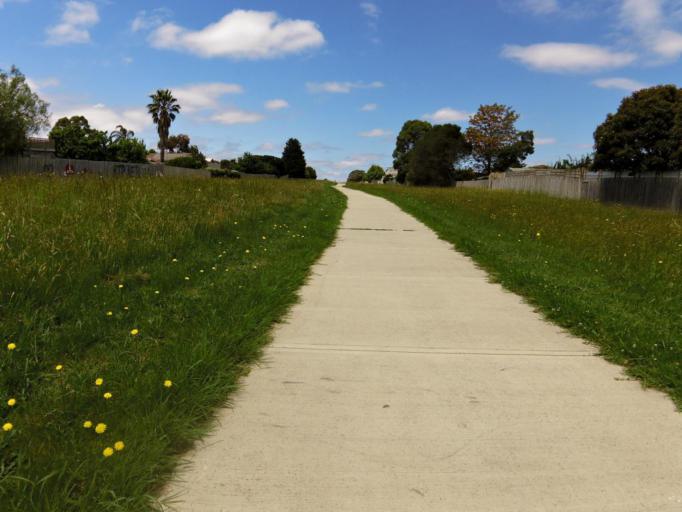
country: AU
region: Victoria
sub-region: Casey
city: Endeavour Hills
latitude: -37.9702
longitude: 145.2693
